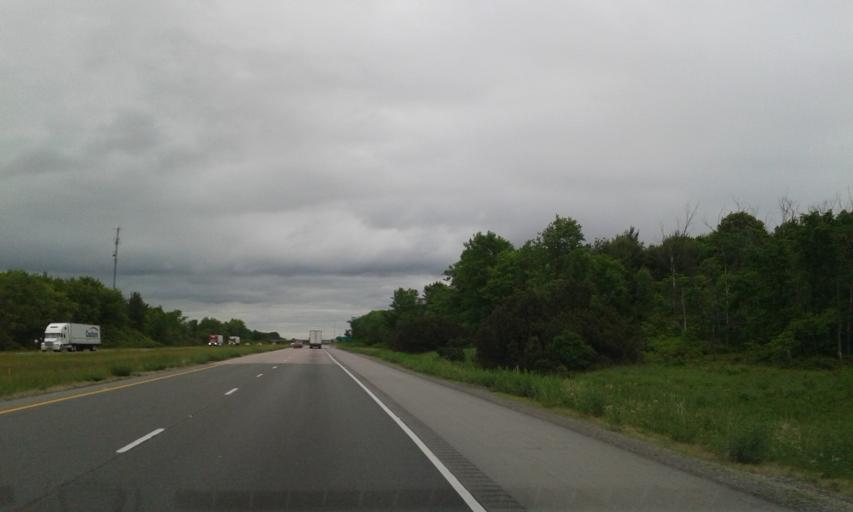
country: US
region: New York
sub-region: Jefferson County
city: Alexandria Bay
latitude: 44.4659
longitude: -75.8761
